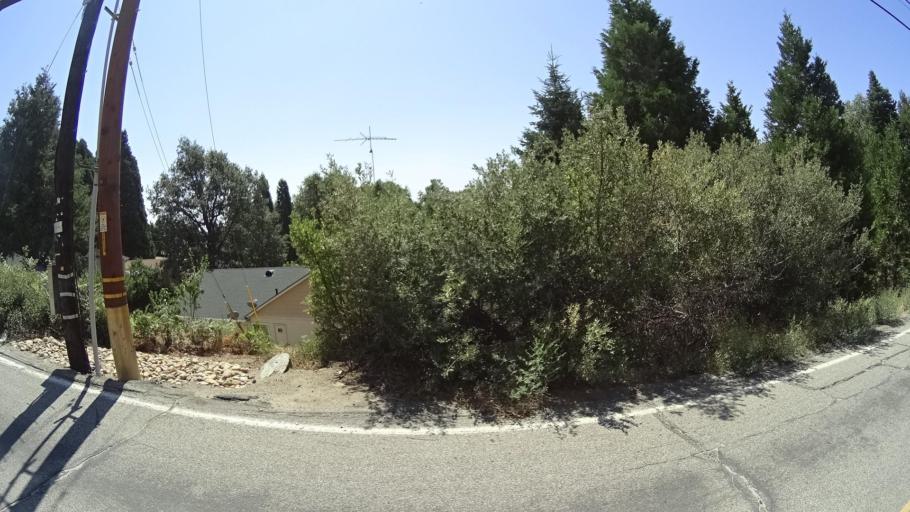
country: US
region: California
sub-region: Riverside County
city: Aguanga
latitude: 33.3099
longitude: -116.8510
